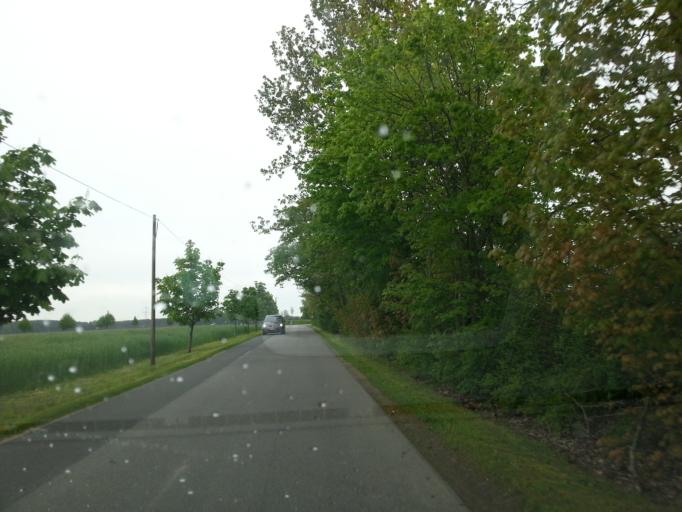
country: DE
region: Mecklenburg-Vorpommern
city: Malchow
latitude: 53.5190
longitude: 12.4196
